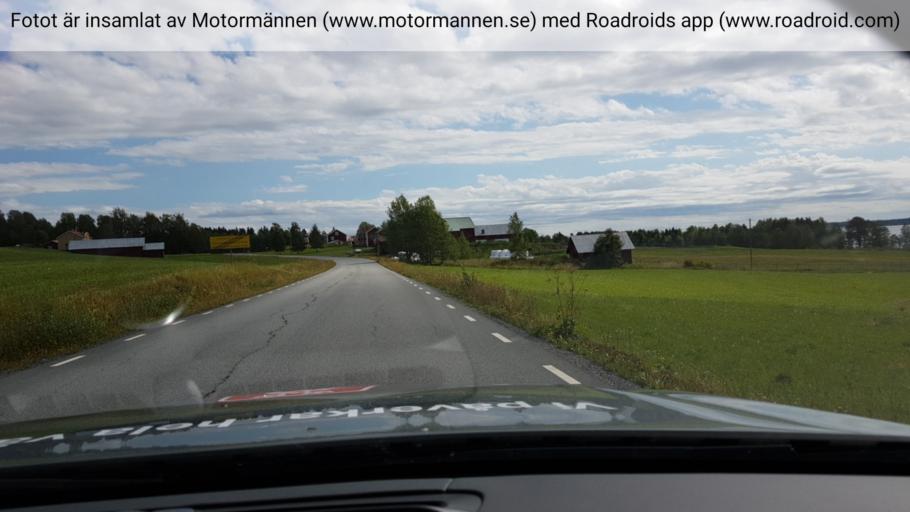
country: SE
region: Jaemtland
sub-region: Krokoms Kommun
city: Valla
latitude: 63.3265
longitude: 14.0340
